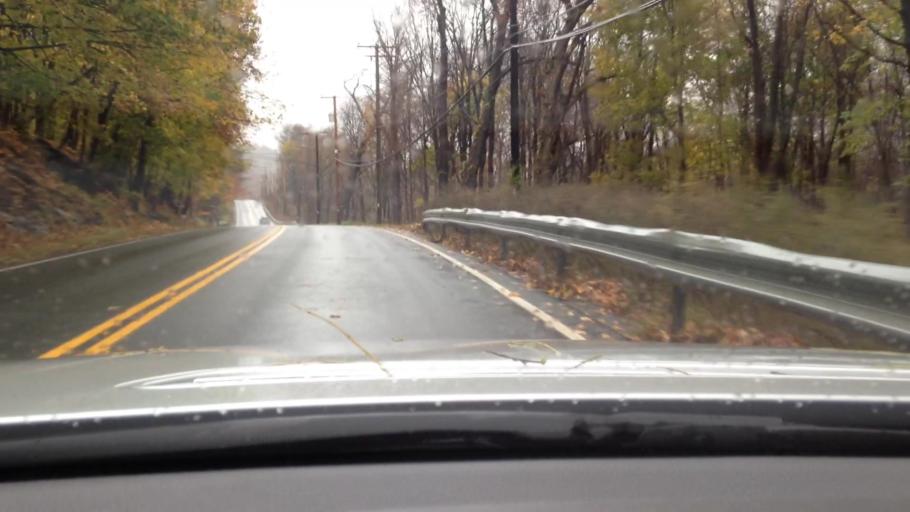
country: US
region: New York
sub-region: Putnam County
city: Cold Spring
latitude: 41.4091
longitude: -73.9345
